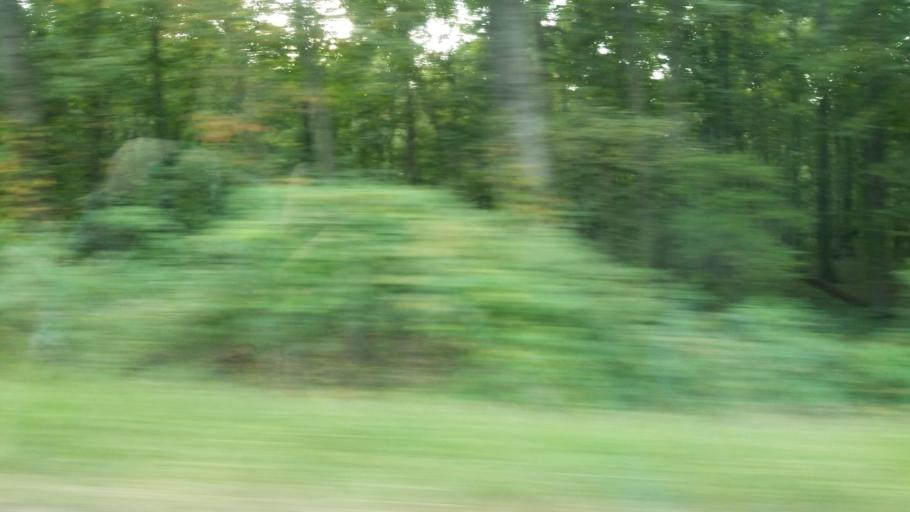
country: US
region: Illinois
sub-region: Saline County
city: Harrisburg
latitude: 37.7801
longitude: -88.5401
